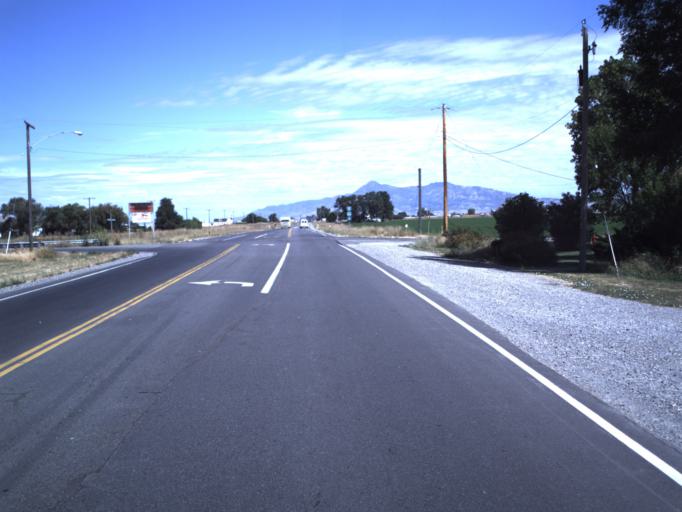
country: US
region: Utah
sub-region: Box Elder County
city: Elwood
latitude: 41.6970
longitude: -112.1417
